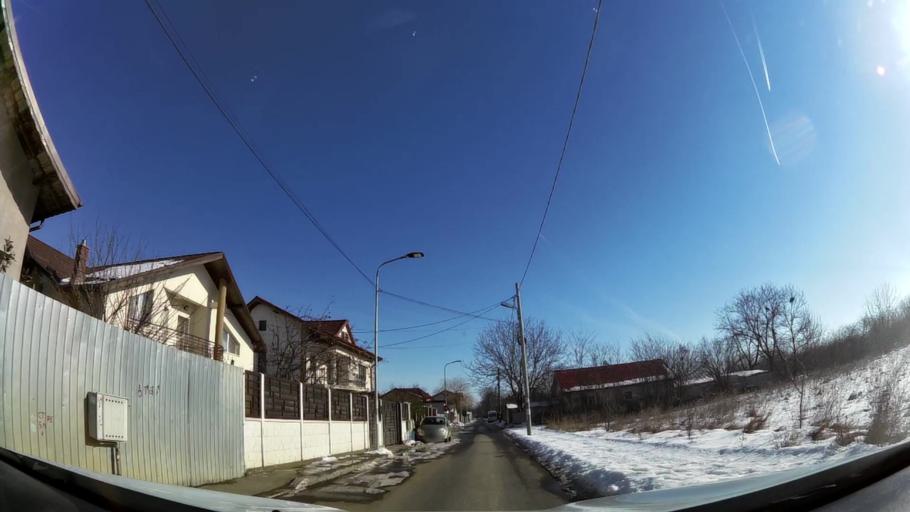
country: RO
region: Ilfov
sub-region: Comuna Magurele
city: Magurele
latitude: 44.3831
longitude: 26.0487
